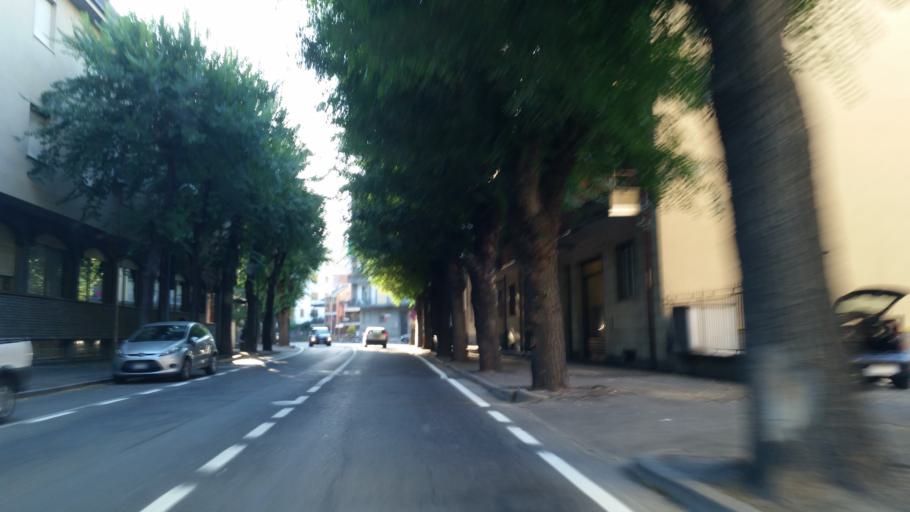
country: IT
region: Piedmont
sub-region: Provincia di Asti
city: Canelli
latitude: 44.7181
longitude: 8.2830
